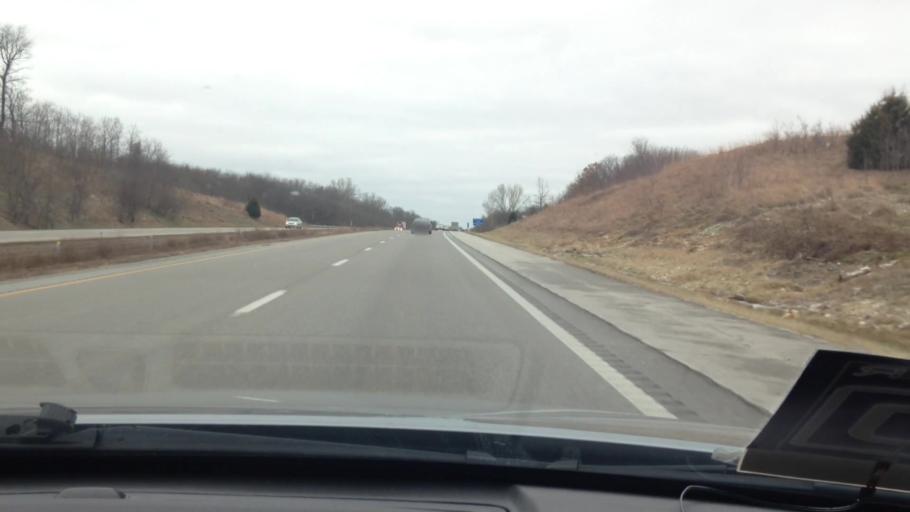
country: US
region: Missouri
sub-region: Platte County
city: Platte City
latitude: 39.4963
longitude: -94.7863
